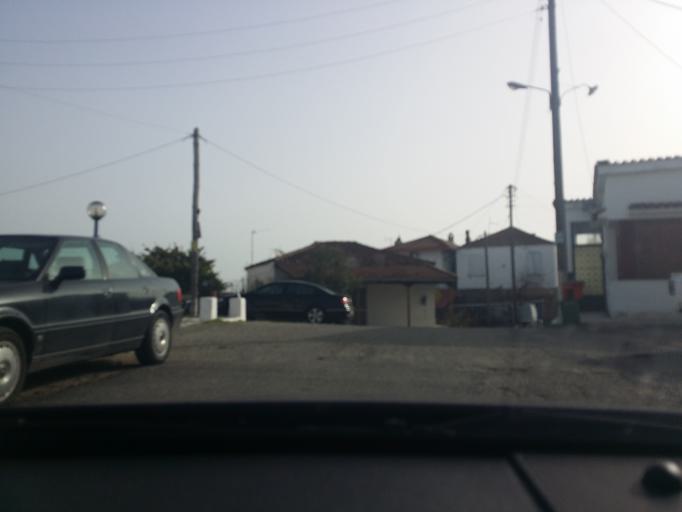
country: GR
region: West Greece
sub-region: Nomos Aitolias kai Akarnanias
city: Katouna
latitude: 38.8267
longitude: 21.0758
